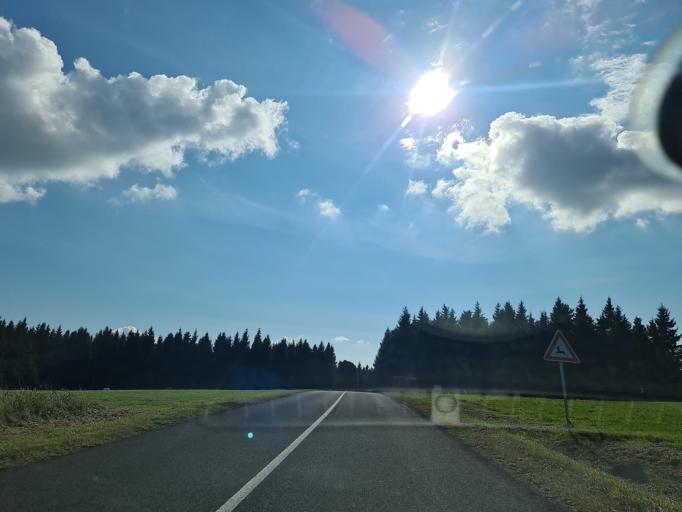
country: CZ
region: Ustecky
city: Mezibori
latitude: 50.6371
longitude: 13.5440
